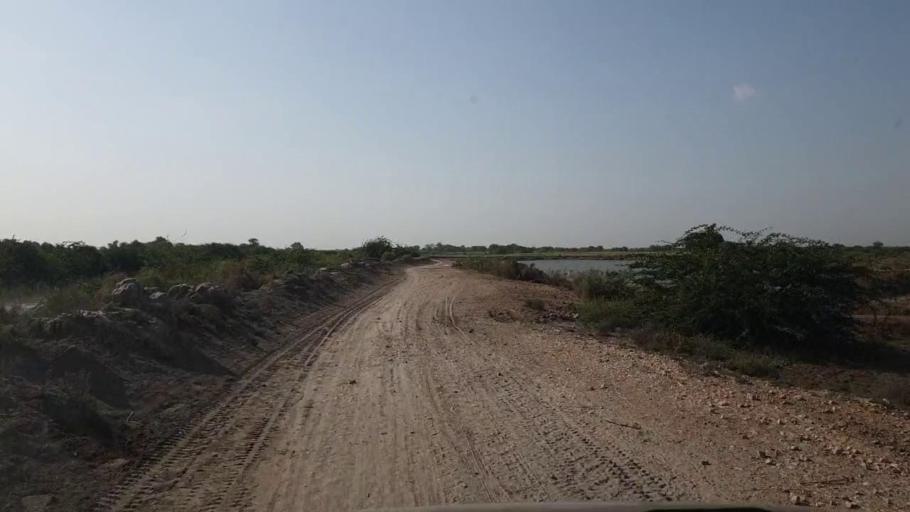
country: PK
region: Sindh
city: Kadhan
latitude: 24.6242
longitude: 69.0731
